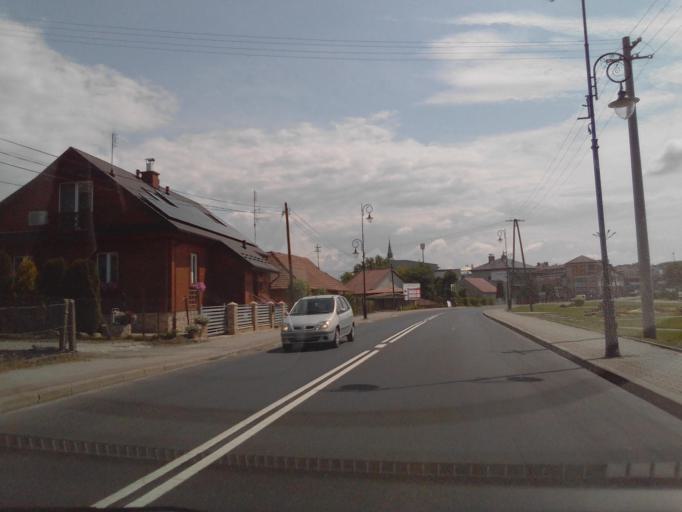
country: PL
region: Subcarpathian Voivodeship
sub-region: Powiat ropczycko-sedziszowski
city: Ropczyce
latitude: 50.0537
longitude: 21.6049
